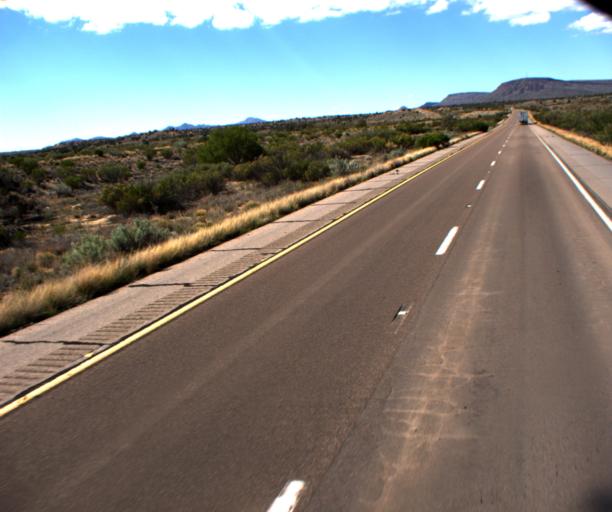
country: US
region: Arizona
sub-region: Mohave County
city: Kingman
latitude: 35.1203
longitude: -113.6662
